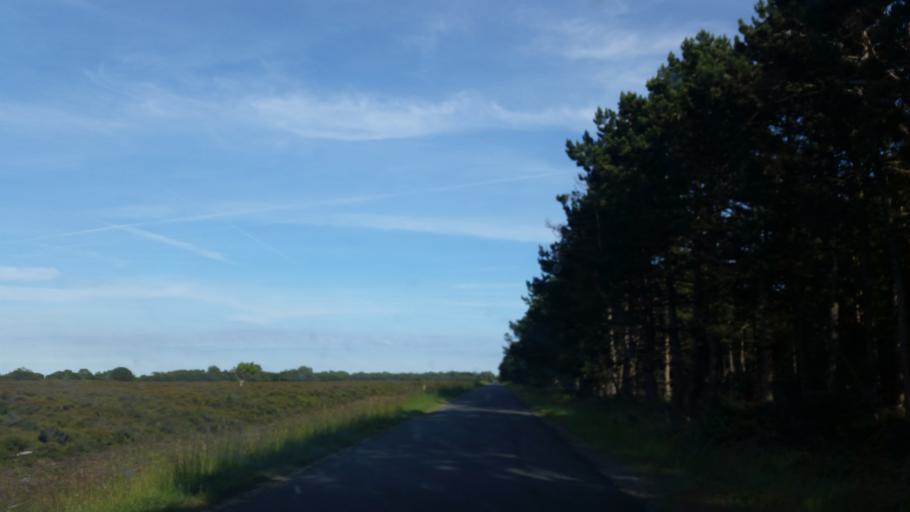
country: DK
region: Central Jutland
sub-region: Samso Kommune
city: Tranebjerg
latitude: 55.9252
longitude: 10.5964
